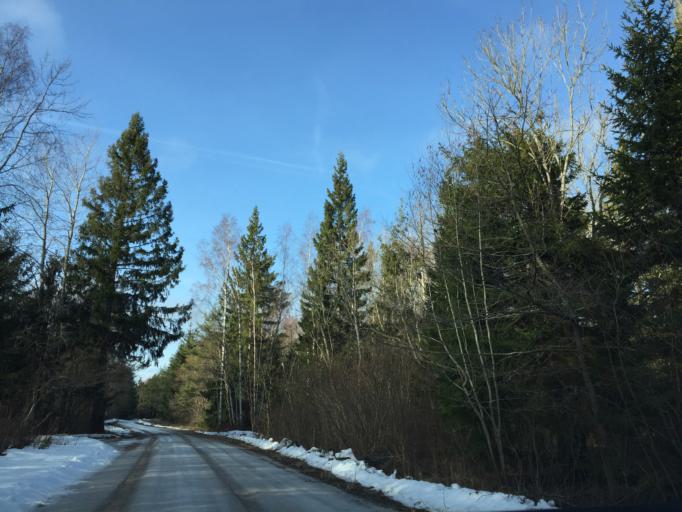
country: EE
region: Saare
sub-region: Kuressaare linn
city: Kuressaare
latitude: 58.4688
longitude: 21.9800
